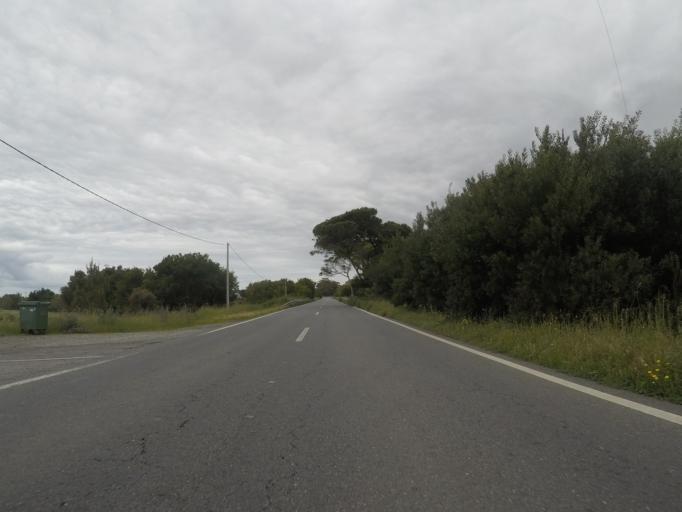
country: PT
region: Beja
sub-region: Odemira
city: Vila Nova de Milfontes
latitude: 37.6974
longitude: -8.7696
